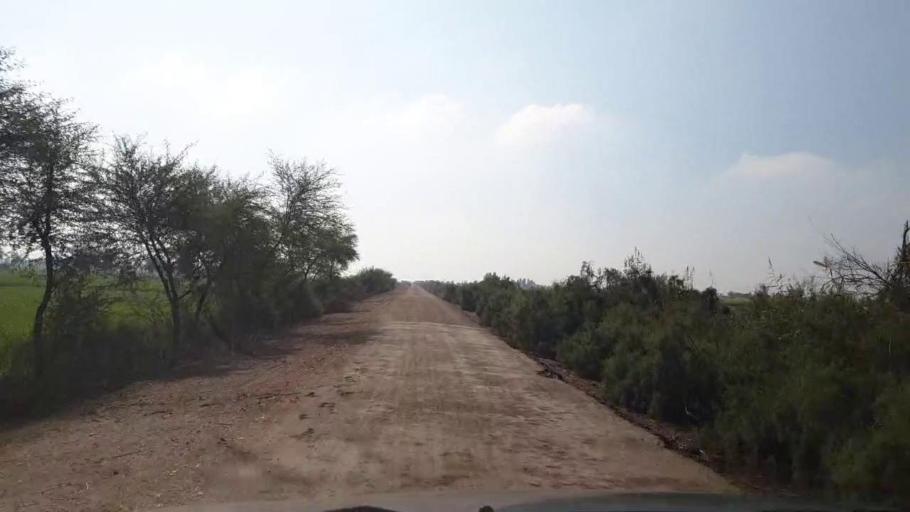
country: PK
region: Sindh
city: Sinjhoro
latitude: 26.0487
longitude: 68.7782
